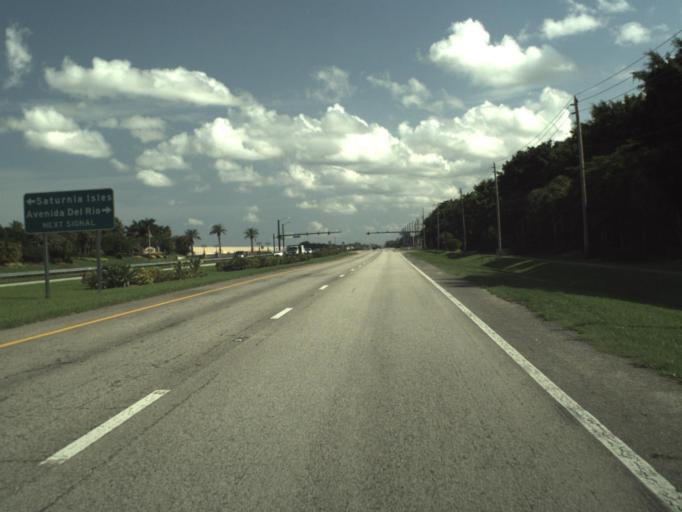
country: US
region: Florida
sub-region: Palm Beach County
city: Villages of Oriole
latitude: 26.4411
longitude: -80.2046
